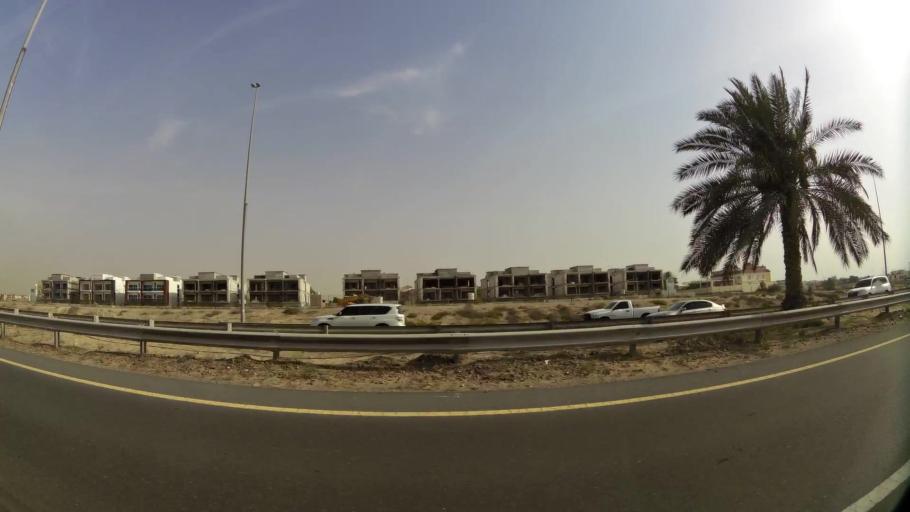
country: AE
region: Ash Shariqah
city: Sharjah
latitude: 25.2343
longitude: 55.4296
